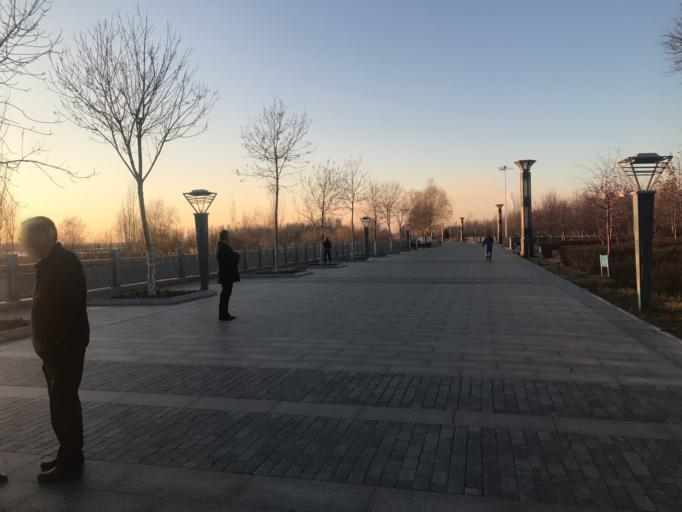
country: CN
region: Xinjiang Uygur Zizhiqu
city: Taxkowruek
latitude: 43.8906
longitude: 81.2871
